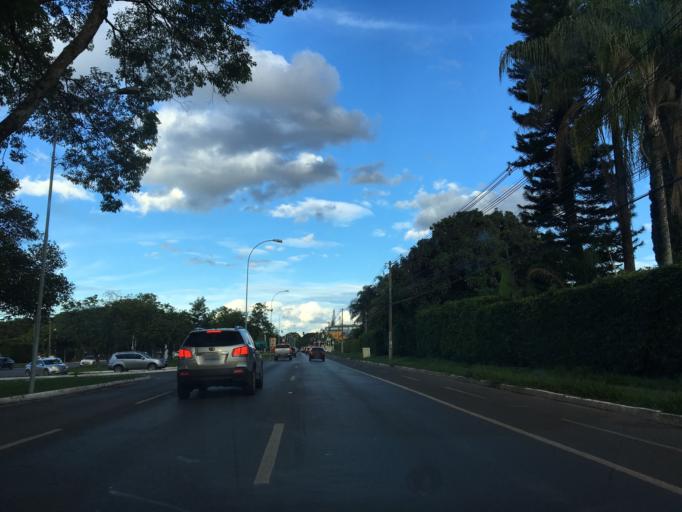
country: BR
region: Federal District
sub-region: Brasilia
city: Brasilia
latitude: -15.8465
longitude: -47.8983
